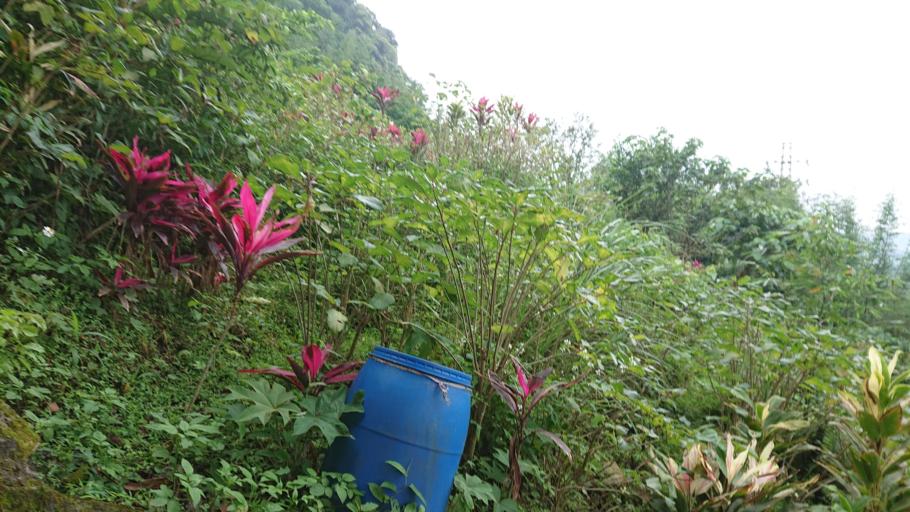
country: TW
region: Taiwan
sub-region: Taoyuan
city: Taoyuan
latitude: 24.9294
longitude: 121.3450
